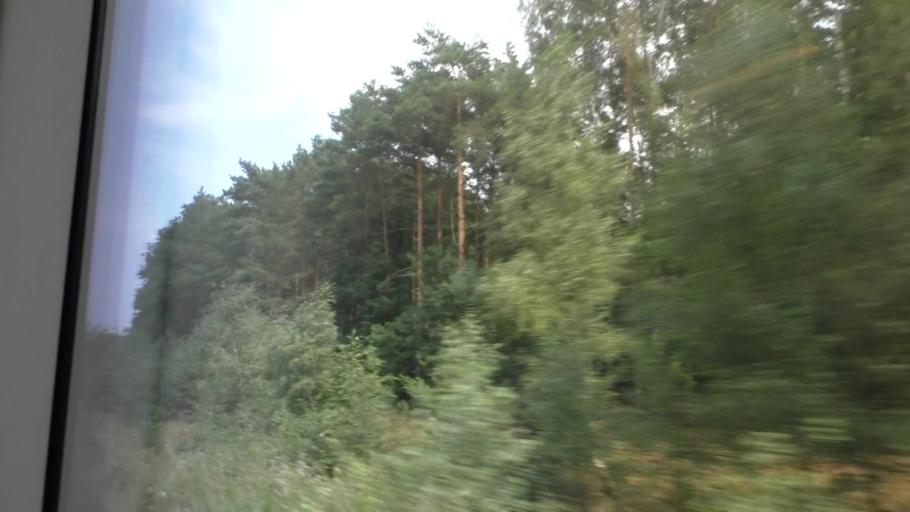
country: DE
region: Brandenburg
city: Mixdorf
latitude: 52.1986
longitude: 14.3952
